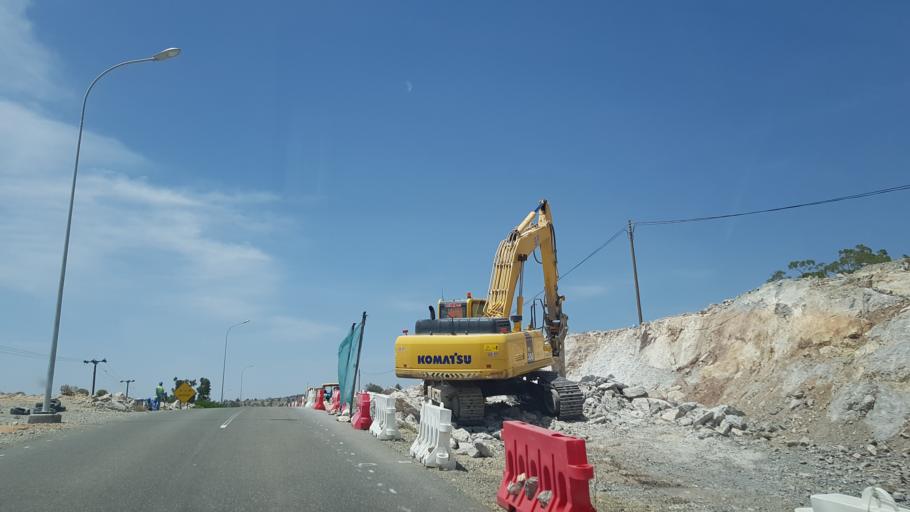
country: OM
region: Muhafazat ad Dakhiliyah
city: Nizwa
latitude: 23.1175
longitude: 57.6374
